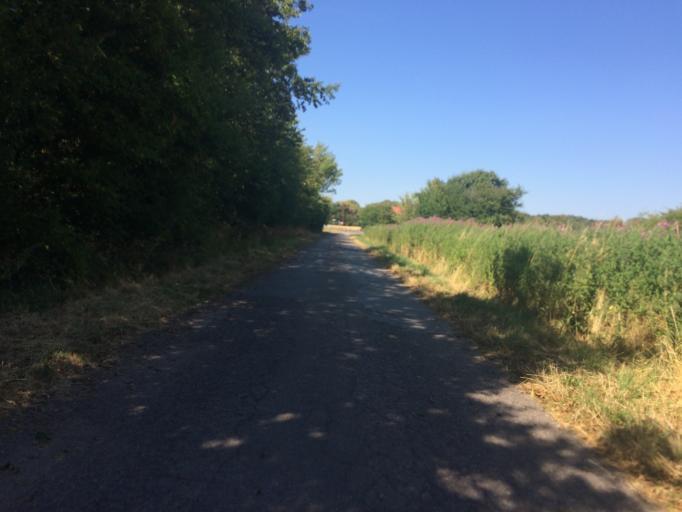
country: DK
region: Central Jutland
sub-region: Holstebro Kommune
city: Vinderup
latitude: 56.5810
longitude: 8.8270
